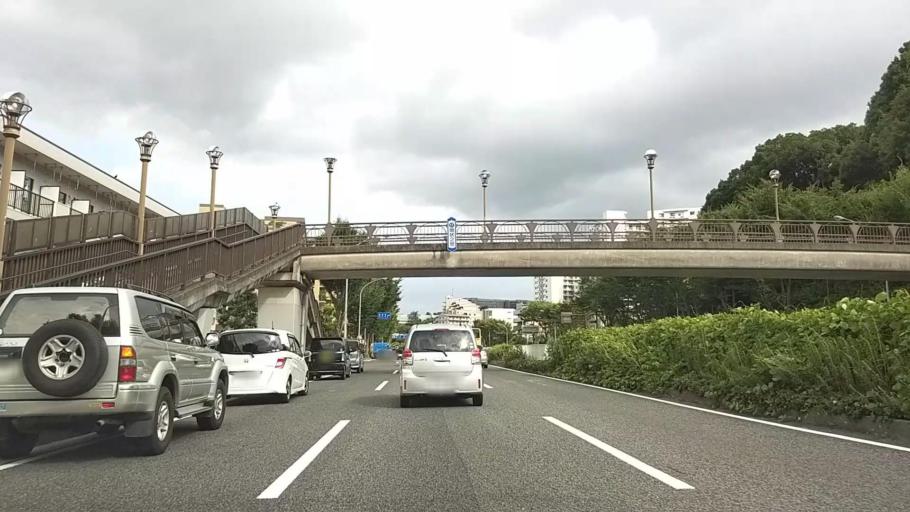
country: JP
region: Kanagawa
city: Yokohama
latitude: 35.4042
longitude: 139.5709
